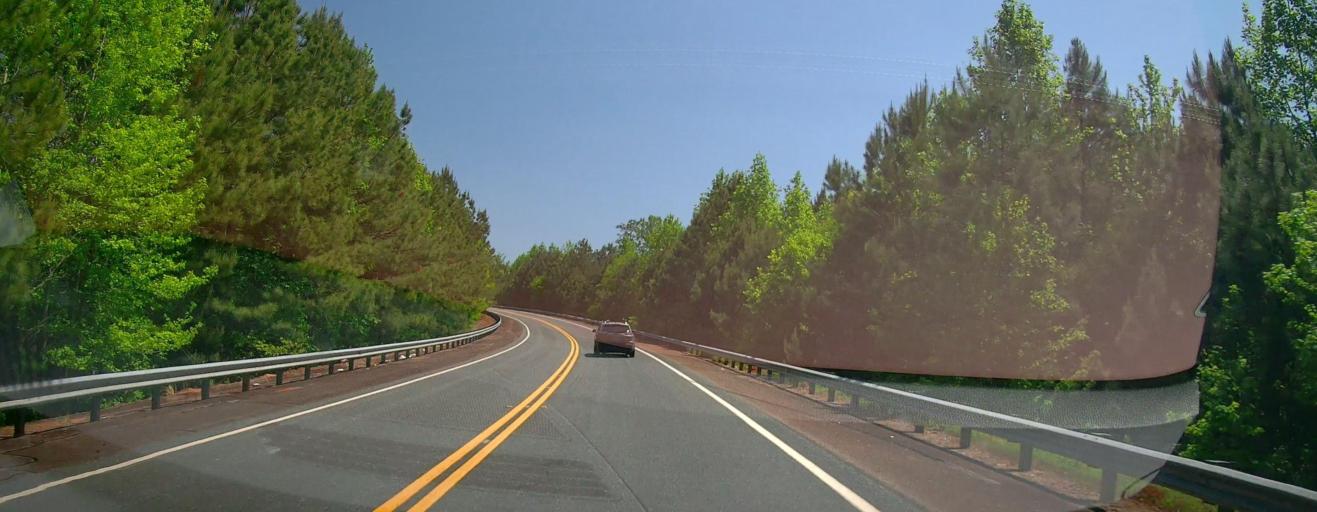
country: US
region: Georgia
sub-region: Jasper County
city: Monticello
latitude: 33.2972
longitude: -83.6640
